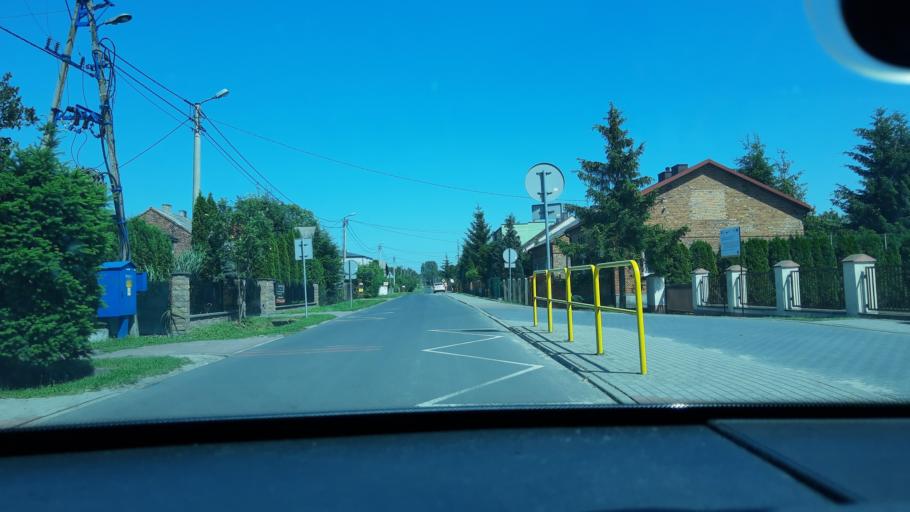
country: PL
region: Lodz Voivodeship
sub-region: Powiat zdunskowolski
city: Zdunska Wola
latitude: 51.6210
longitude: 18.9534
